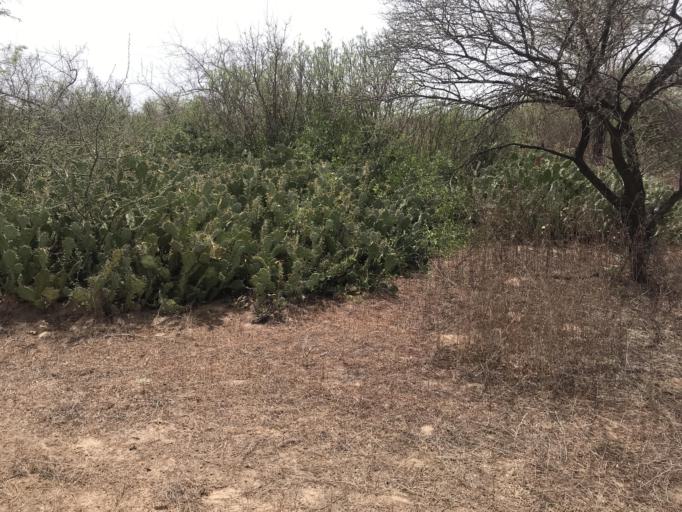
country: SN
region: Saint-Louis
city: Saint-Louis
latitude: 15.9129
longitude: -16.4553
